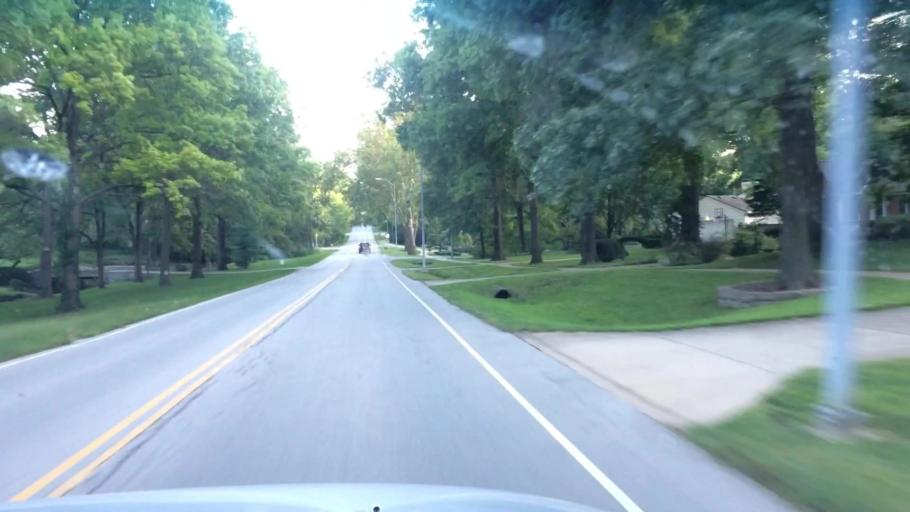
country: US
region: Kansas
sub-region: Johnson County
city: Leawood
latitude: 38.9743
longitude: -94.6141
